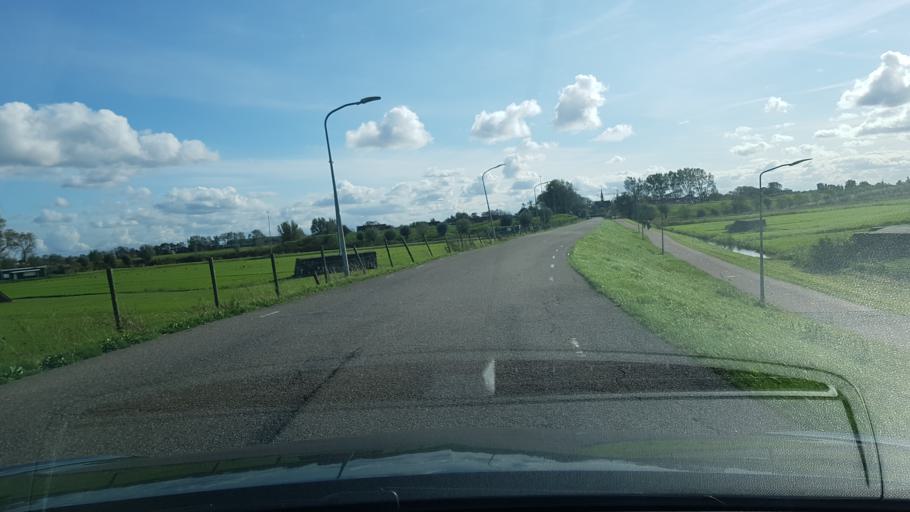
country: NL
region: North Holland
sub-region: Gemeente Velsen
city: Velsen-Zuid
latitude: 52.4193
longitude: 4.6736
